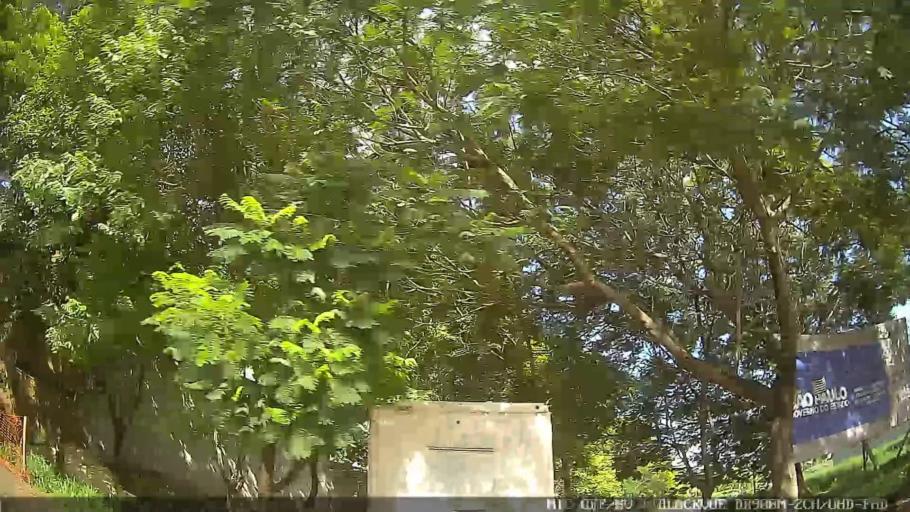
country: BR
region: Sao Paulo
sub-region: Jaguariuna
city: Jaguariuna
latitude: -22.6271
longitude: -47.0520
